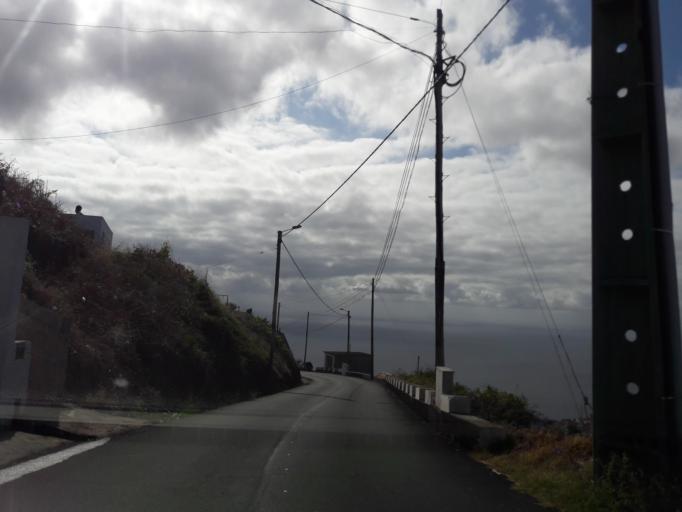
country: PT
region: Madeira
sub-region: Santa Cruz
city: Camacha
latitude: 32.6581
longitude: -16.8382
